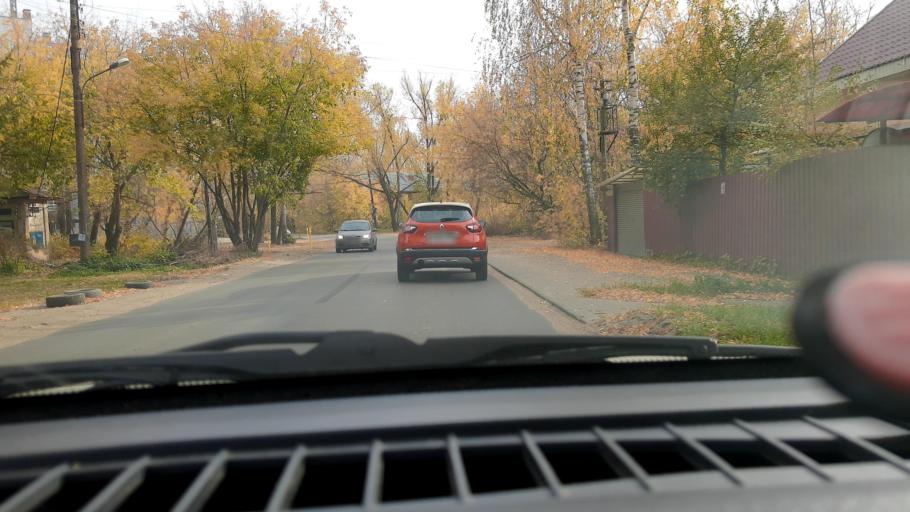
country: RU
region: Nizjnij Novgorod
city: Gorbatovka
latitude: 56.3447
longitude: 43.8301
